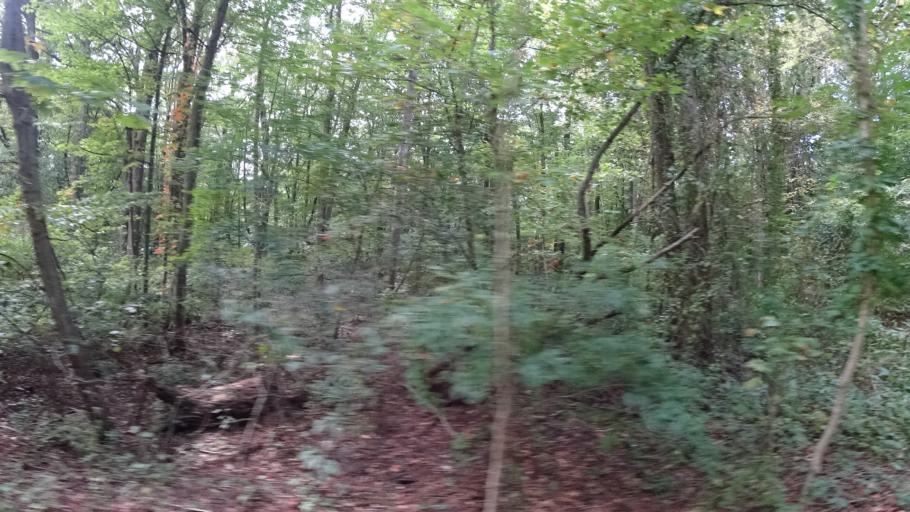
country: US
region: Indiana
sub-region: LaPorte County
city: Long Beach
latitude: 41.7261
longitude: -86.8505
